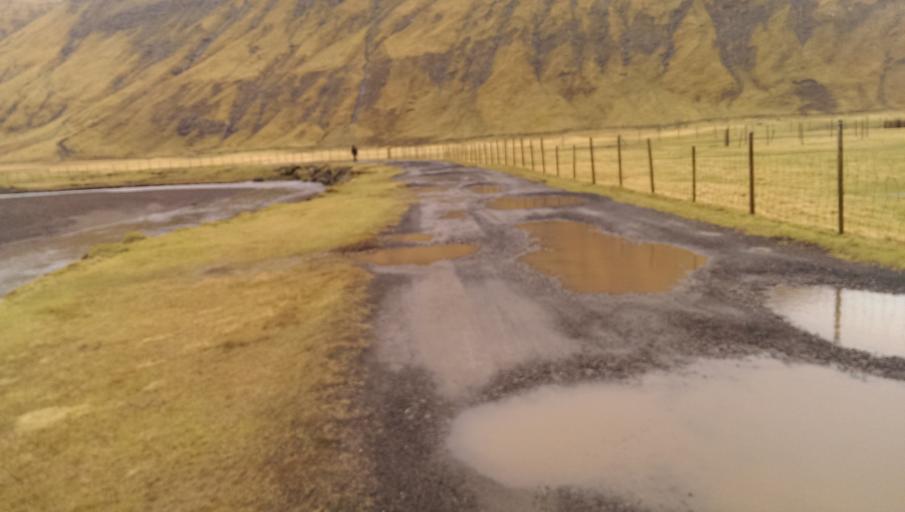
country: FO
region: Streymoy
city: Kollafjordhur
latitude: 62.1314
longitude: -7.0238
